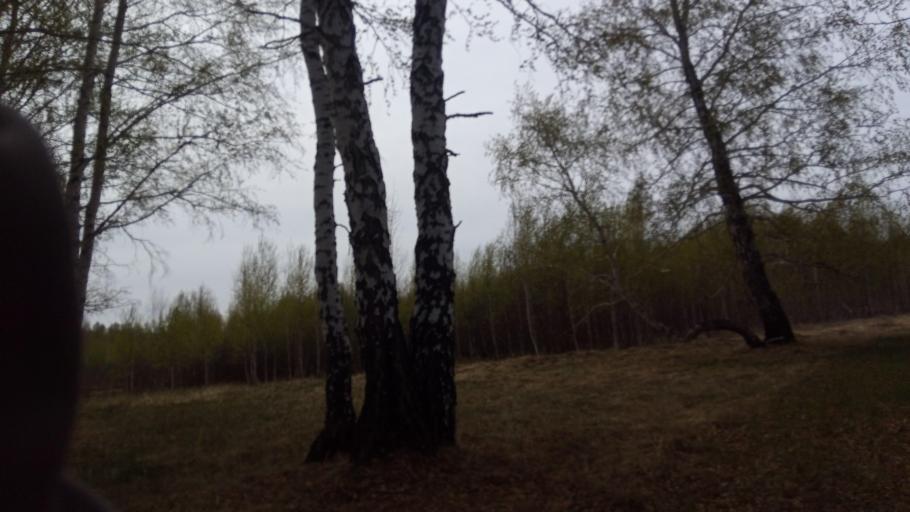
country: RU
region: Chelyabinsk
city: Timiryazevskiy
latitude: 54.9982
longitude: 60.8513
